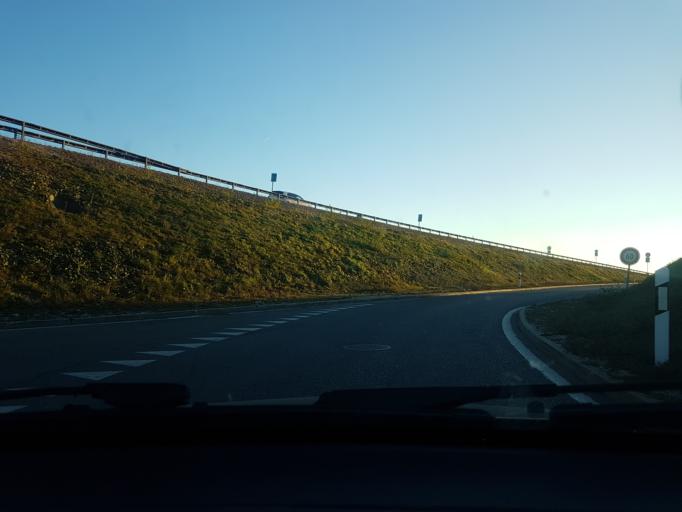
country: CH
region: Neuchatel
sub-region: Le Locle District
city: Le Locle
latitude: 47.0742
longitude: 6.7794
